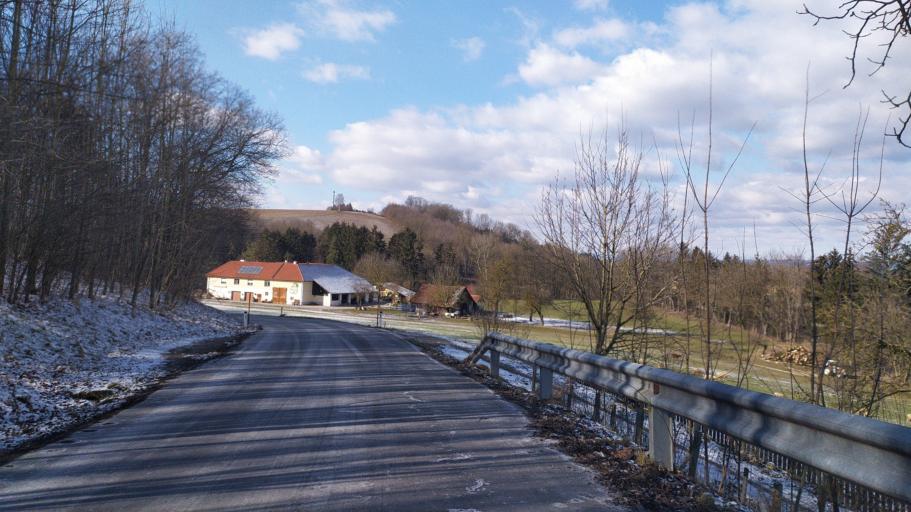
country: AT
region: Lower Austria
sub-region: Politischer Bezirk Amstetten
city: Zeillern
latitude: 48.1557
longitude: 14.7372
